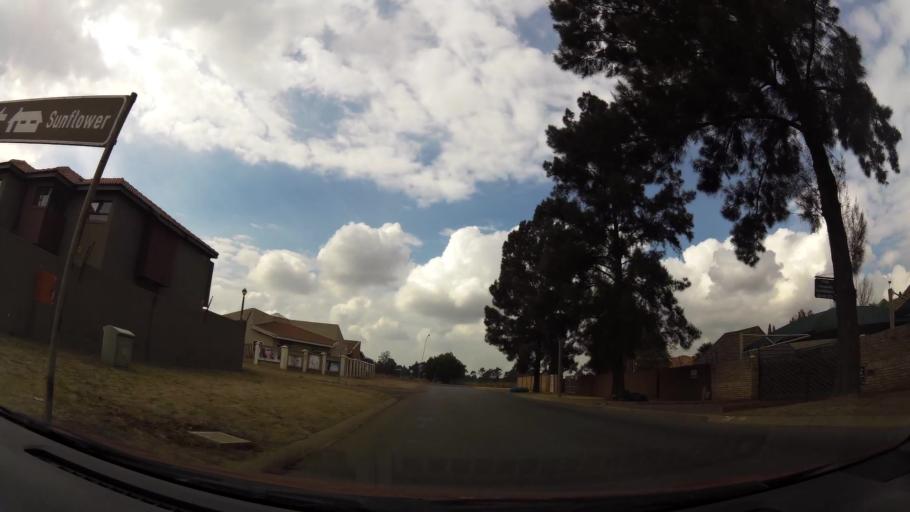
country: ZA
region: Gauteng
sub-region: Sedibeng District Municipality
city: Vanderbijlpark
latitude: -26.7381
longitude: 27.8542
